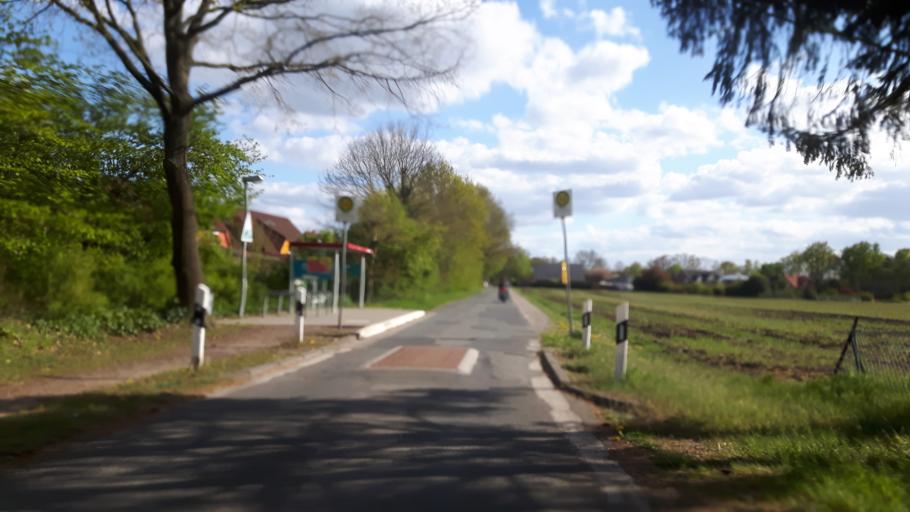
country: DE
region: Lower Saxony
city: Kirchseelte
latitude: 52.9931
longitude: 8.6894
